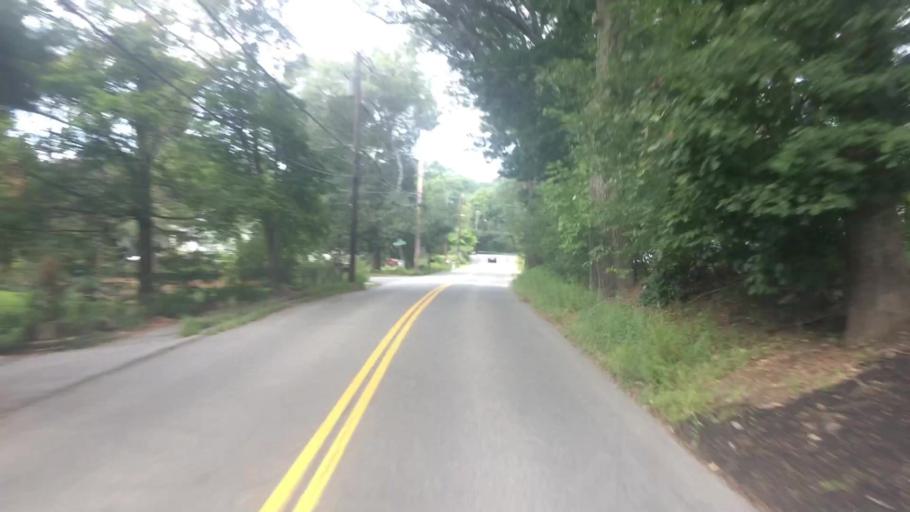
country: US
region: Massachusetts
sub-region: Middlesex County
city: Acton
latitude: 42.4632
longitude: -71.4324
